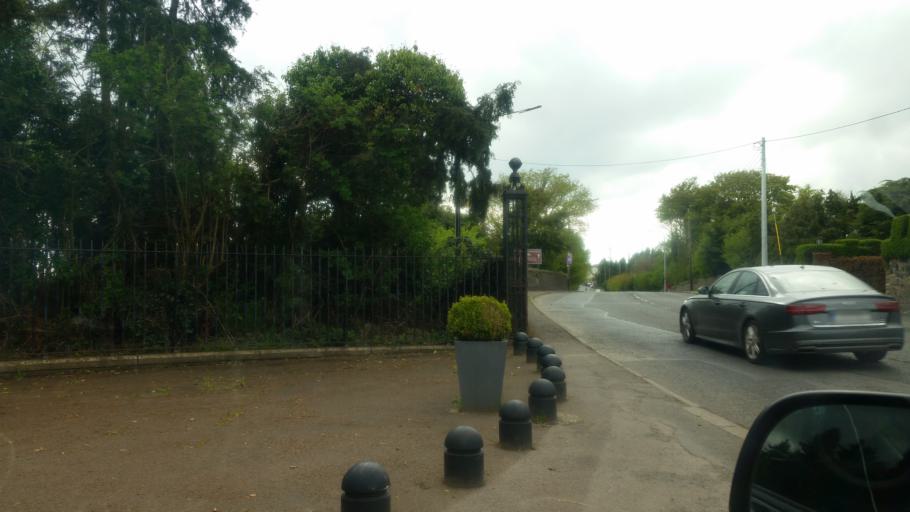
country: IE
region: Leinster
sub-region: Kildare
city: Kildare
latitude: 53.1538
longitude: -6.8999
